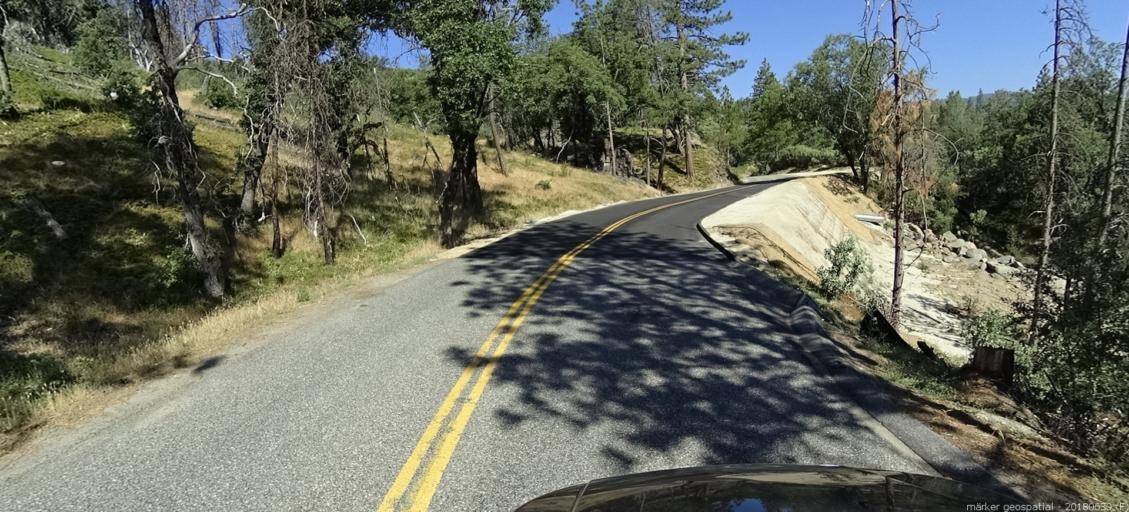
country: US
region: California
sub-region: Fresno County
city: Auberry
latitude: 37.2226
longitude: -119.3546
